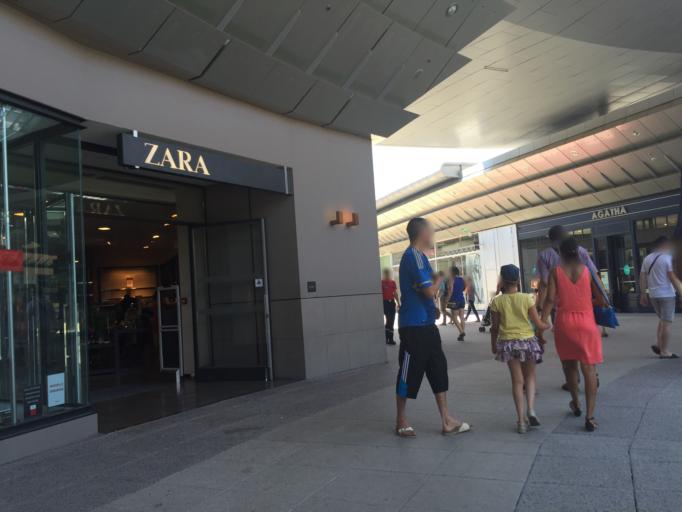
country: FR
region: Languedoc-Roussillon
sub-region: Departement de l'Herault
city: Castelnau-le-Lez
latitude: 43.6042
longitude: 3.9222
